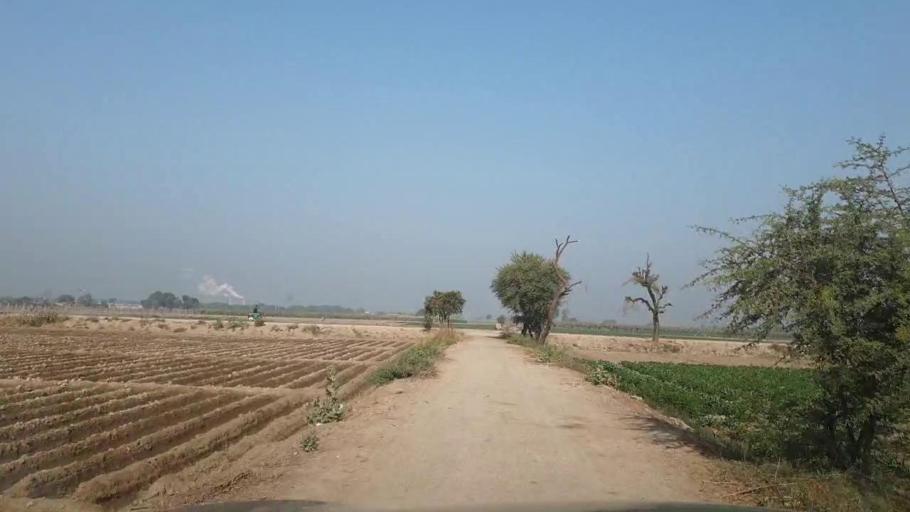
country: PK
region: Sindh
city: Tando Allahyar
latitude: 25.4773
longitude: 68.7369
